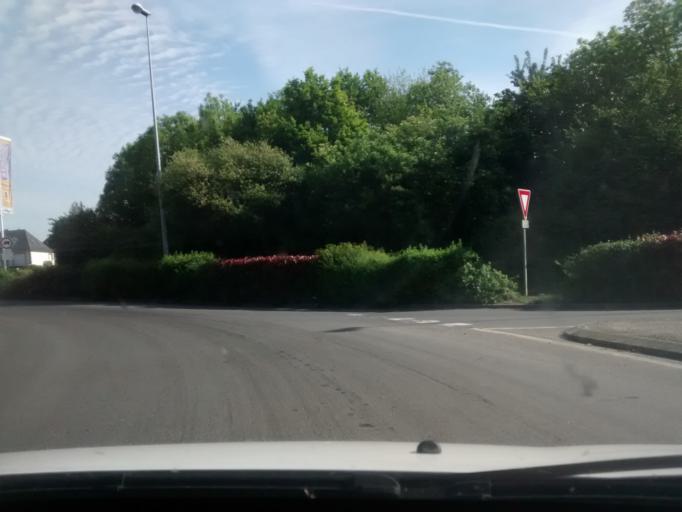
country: FR
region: Brittany
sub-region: Departement d'Ille-et-Vilaine
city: Fougeres
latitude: 48.3384
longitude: -1.2105
